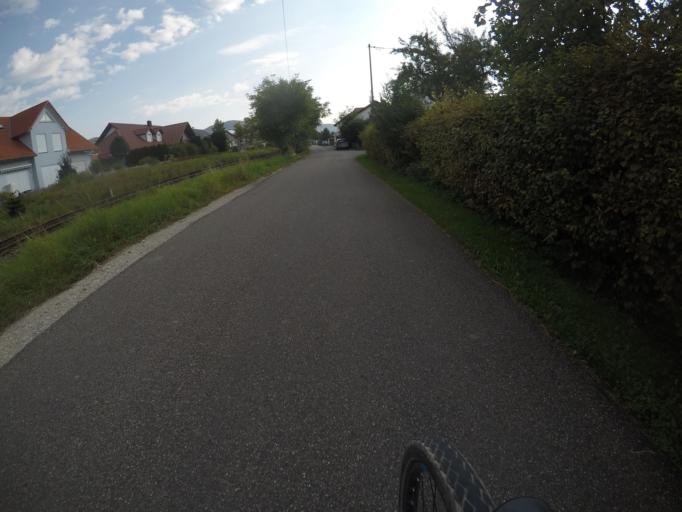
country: DE
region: Baden-Wuerttemberg
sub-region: Tuebingen Region
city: Metzingen
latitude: 48.5325
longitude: 9.3126
